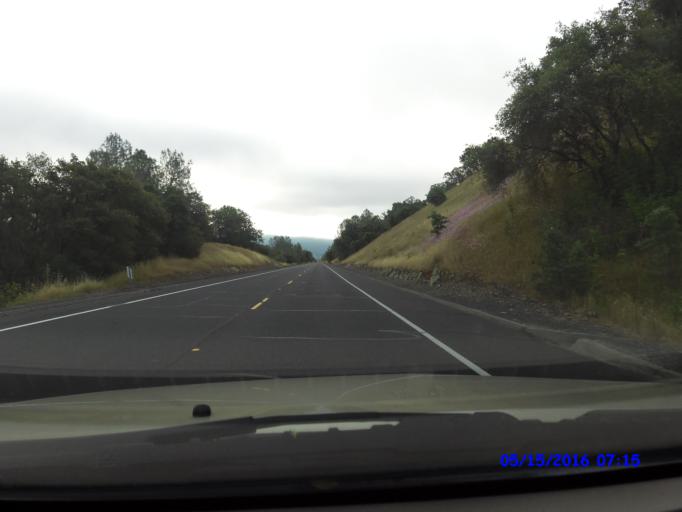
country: US
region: California
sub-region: Tuolumne County
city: East Sonora
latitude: 37.8243
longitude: -120.3346
